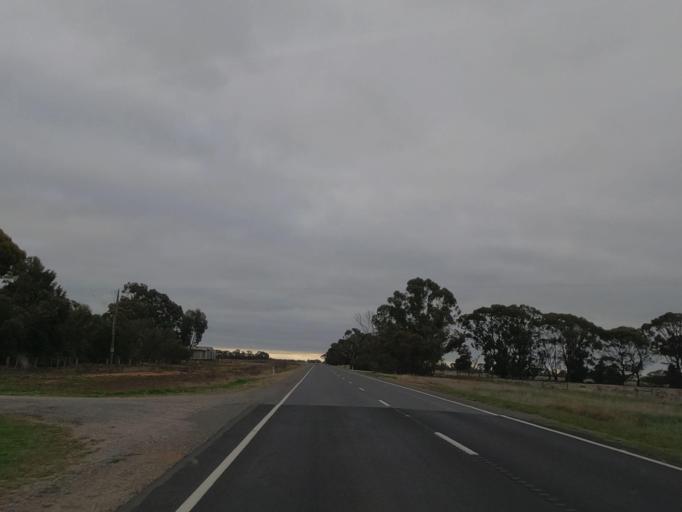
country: AU
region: Victoria
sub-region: Greater Bendigo
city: Long Gully
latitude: -36.0514
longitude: 143.9480
